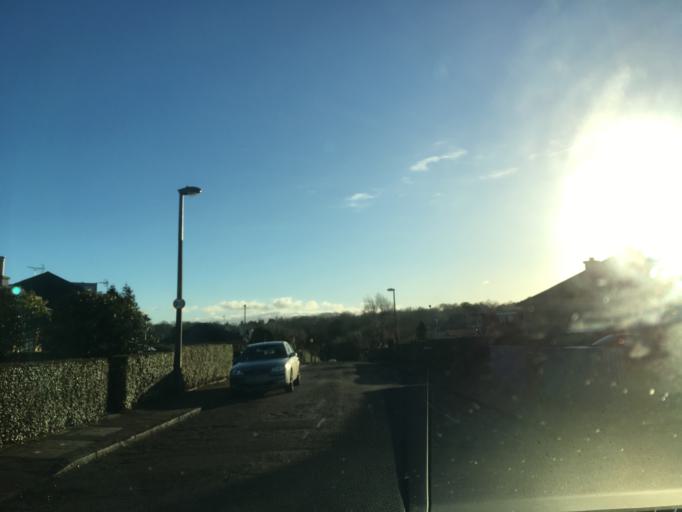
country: GB
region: Scotland
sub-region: Edinburgh
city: Colinton
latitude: 55.9586
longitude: -3.2615
